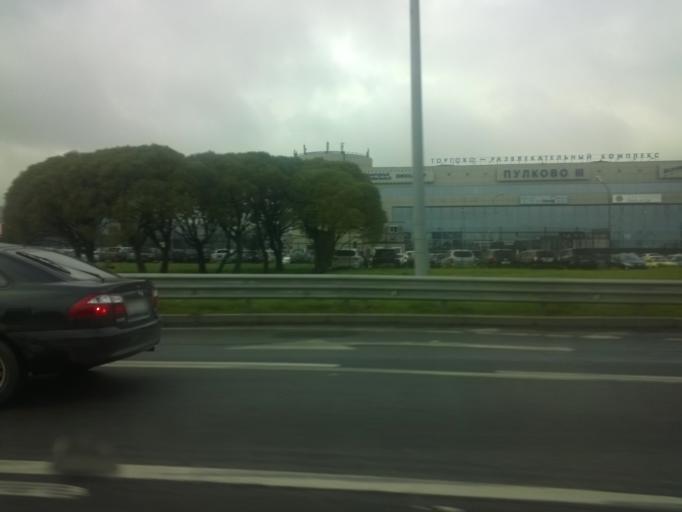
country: RU
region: St.-Petersburg
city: Kupchino
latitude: 59.8057
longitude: 30.3235
